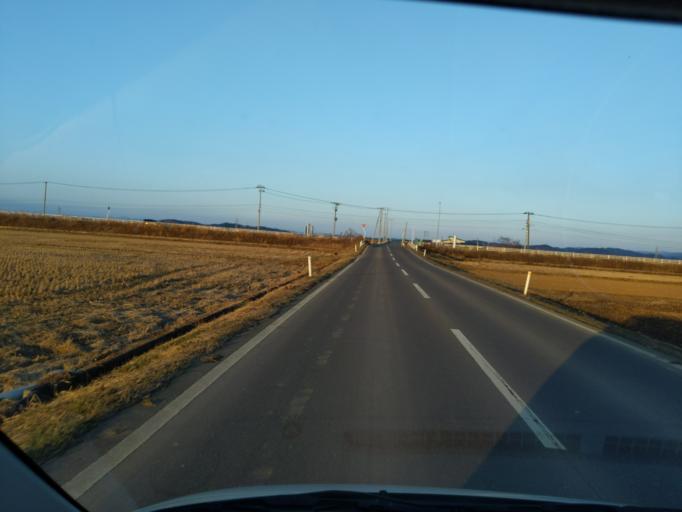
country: JP
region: Miyagi
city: Wakuya
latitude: 38.7180
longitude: 141.1591
